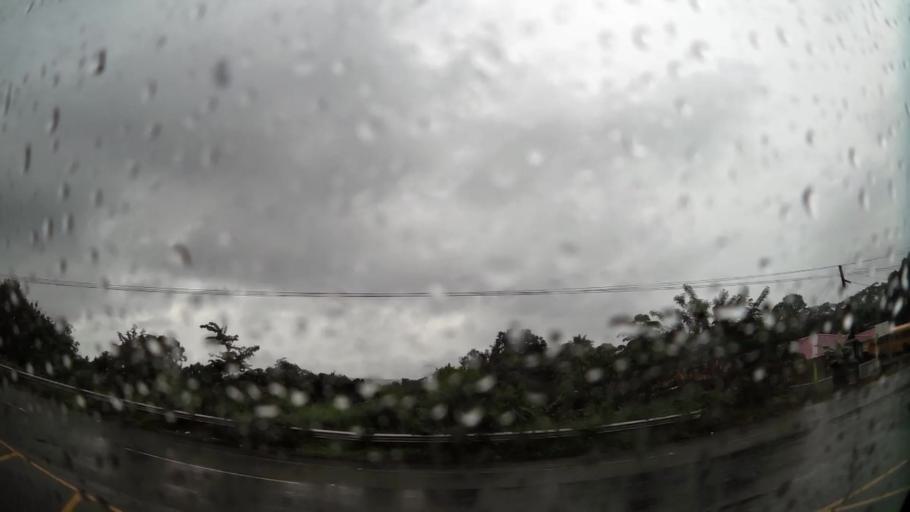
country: PA
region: Colon
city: Quebrada Bonita Adentro
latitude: 9.2839
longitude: -79.7123
